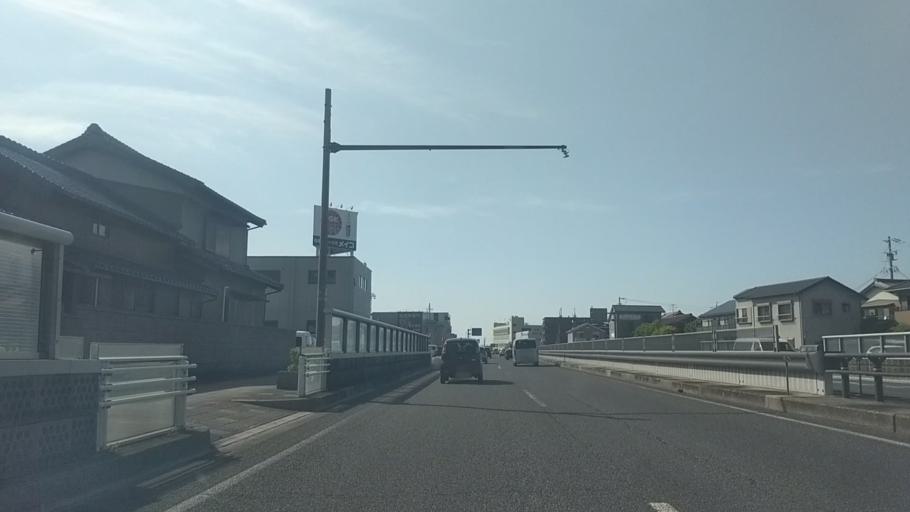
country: JP
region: Aichi
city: Anjo
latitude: 34.9905
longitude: 137.0818
